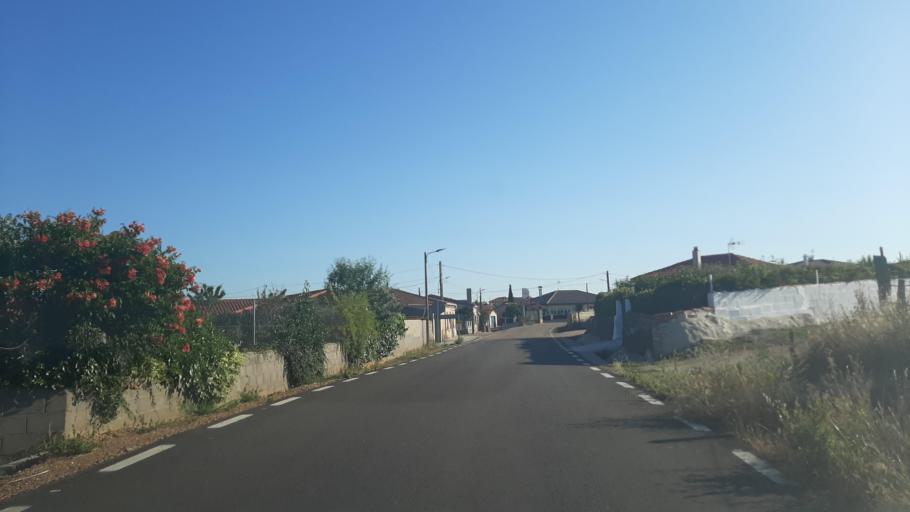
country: ES
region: Castille and Leon
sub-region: Provincia de Salamanca
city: Cabrillas
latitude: 40.6962
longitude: -6.1882
